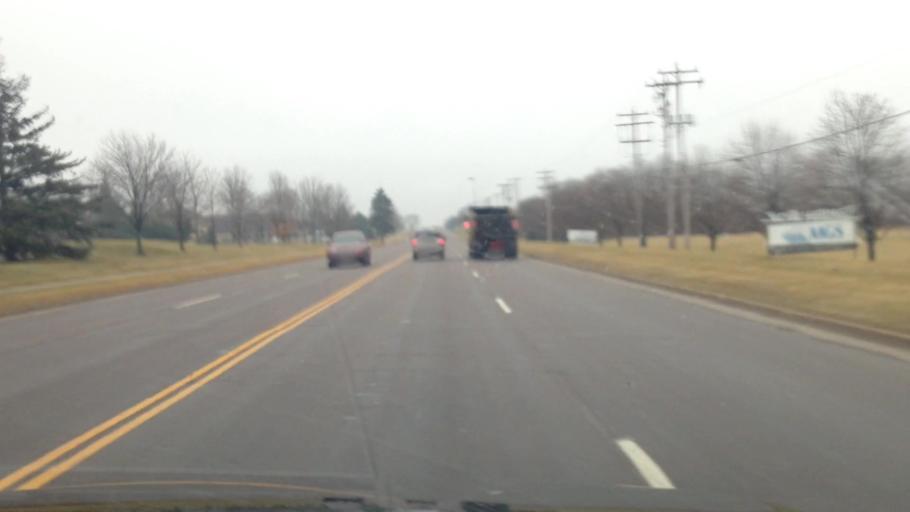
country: US
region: Wisconsin
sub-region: Washington County
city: Germantown
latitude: 43.2305
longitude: -88.1428
